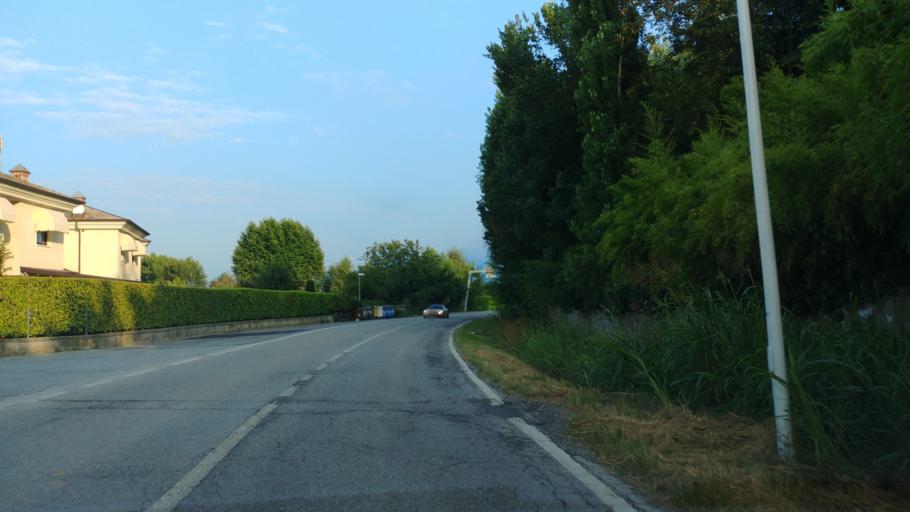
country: IT
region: Piedmont
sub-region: Provincia di Cuneo
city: Cuneo
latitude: 44.3778
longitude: 7.5732
